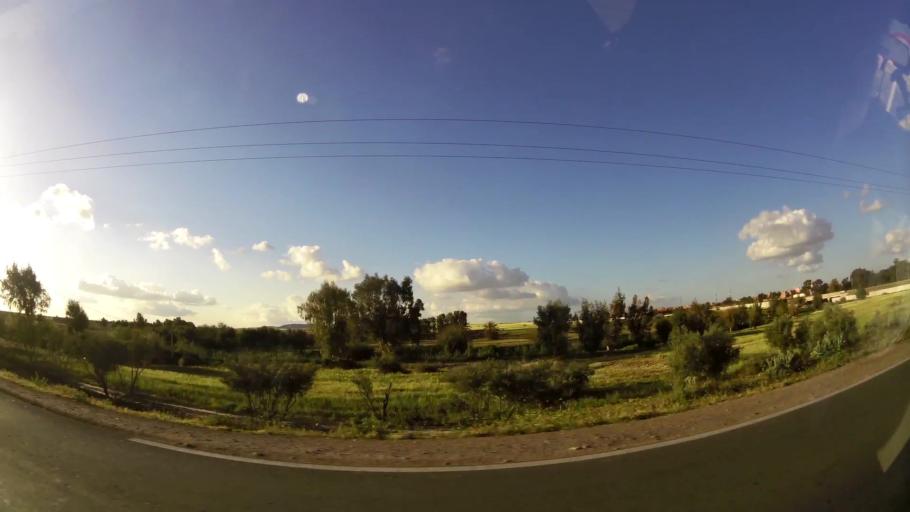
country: MA
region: Marrakech-Tensift-Al Haouz
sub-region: Kelaa-Des-Sraghna
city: Sidi Bou Othmane
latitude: 32.2281
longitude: -7.9670
